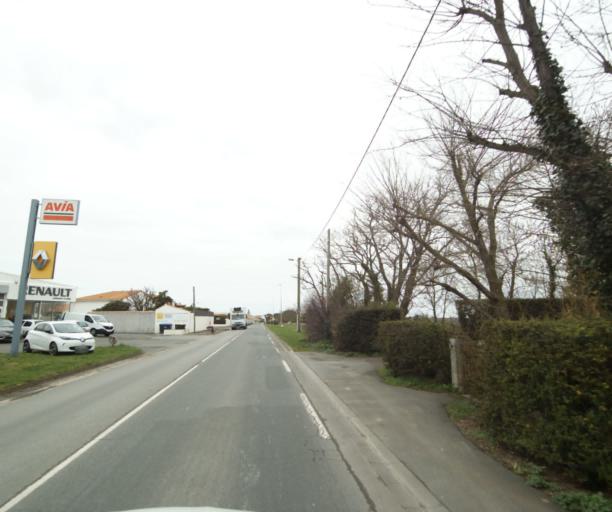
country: FR
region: Poitou-Charentes
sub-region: Departement de la Charente-Maritime
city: Nieul-sur-Mer
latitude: 46.1984
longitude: -1.1585
